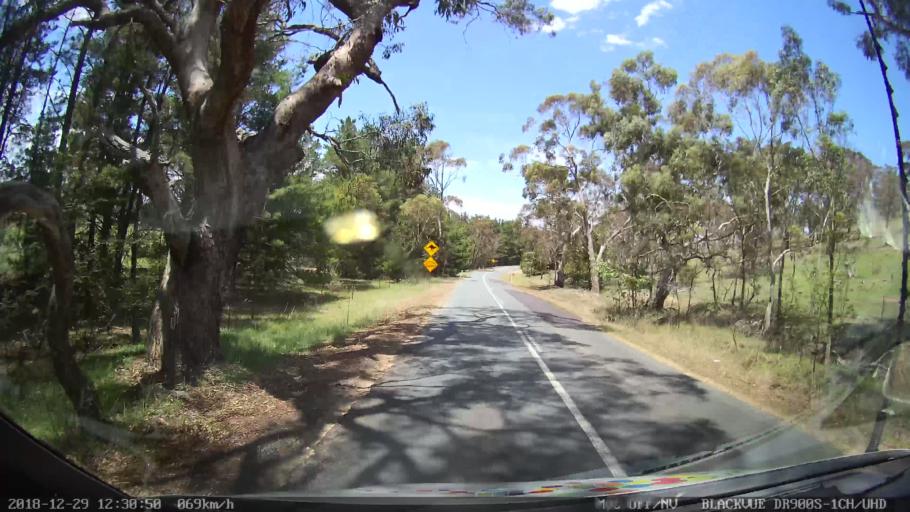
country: AU
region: Australian Capital Territory
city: Macarthur
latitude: -35.5096
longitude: 149.2329
